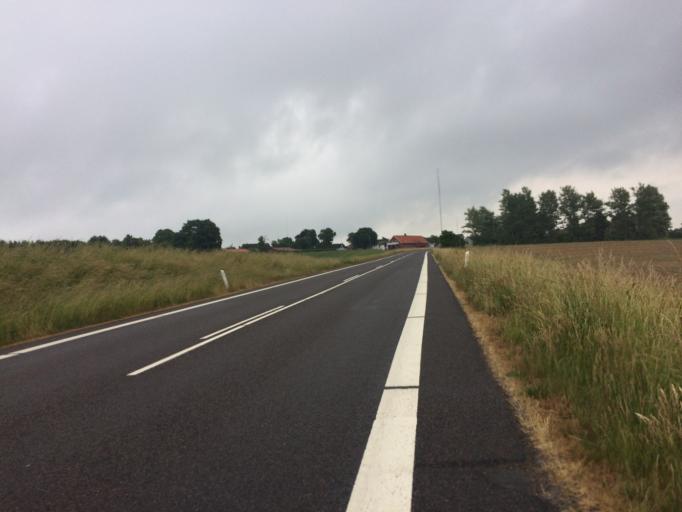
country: DK
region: Capital Region
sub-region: Bornholm Kommune
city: Akirkeby
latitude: 55.1428
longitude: 14.8655
